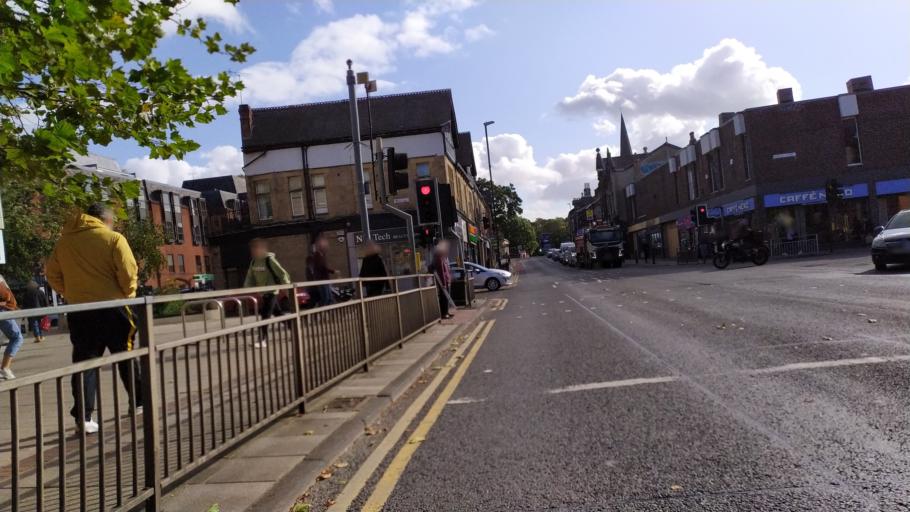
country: GB
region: England
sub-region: City and Borough of Leeds
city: Leeds
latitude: 53.8216
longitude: -1.5779
